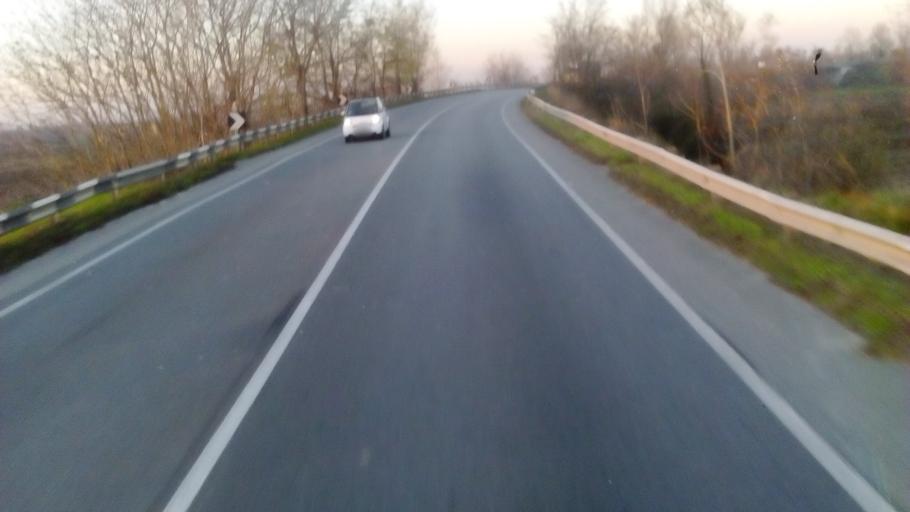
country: IT
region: Lombardy
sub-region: Provincia di Cremona
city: Soncino
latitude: 45.4051
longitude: 9.8569
